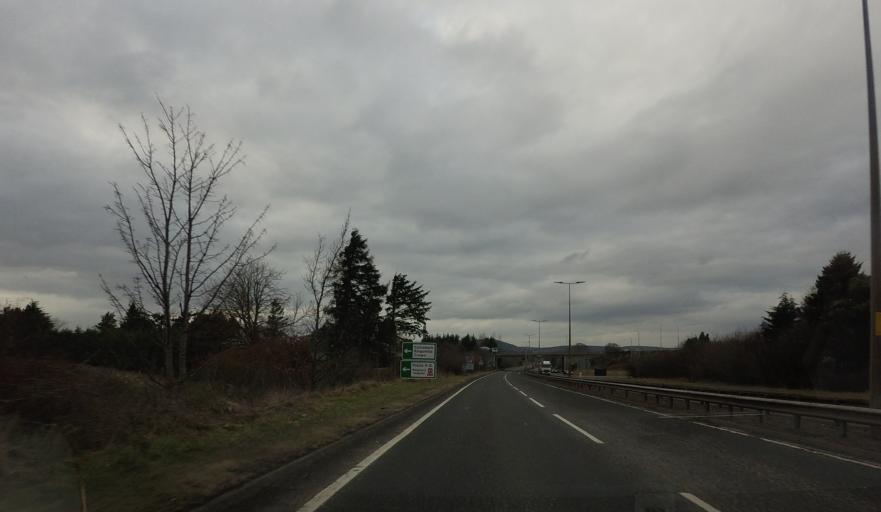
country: GB
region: Scotland
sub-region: Highland
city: Inverness
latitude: 57.4703
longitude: -4.1831
